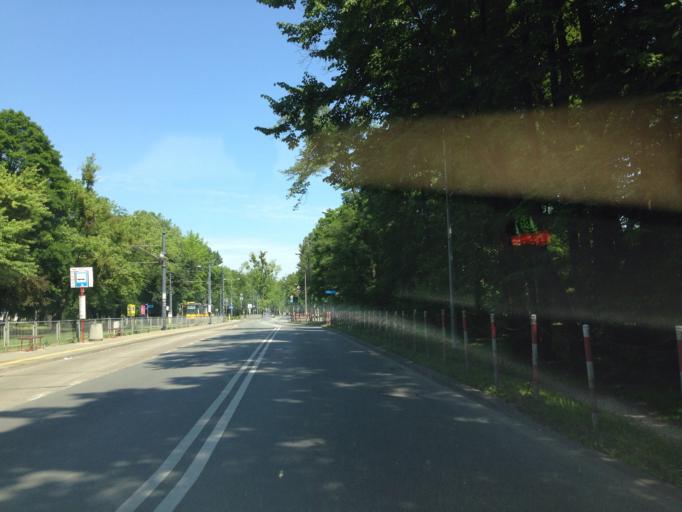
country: PL
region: Masovian Voivodeship
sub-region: Warszawa
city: Bemowo
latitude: 52.2512
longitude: 20.8985
